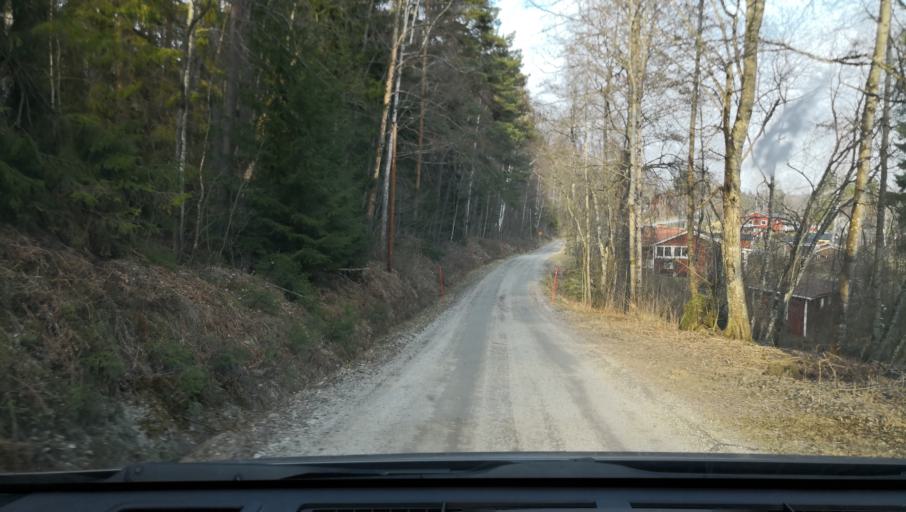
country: SE
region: OErebro
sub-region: Lindesbergs Kommun
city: Frovi
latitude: 59.3936
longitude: 15.3896
